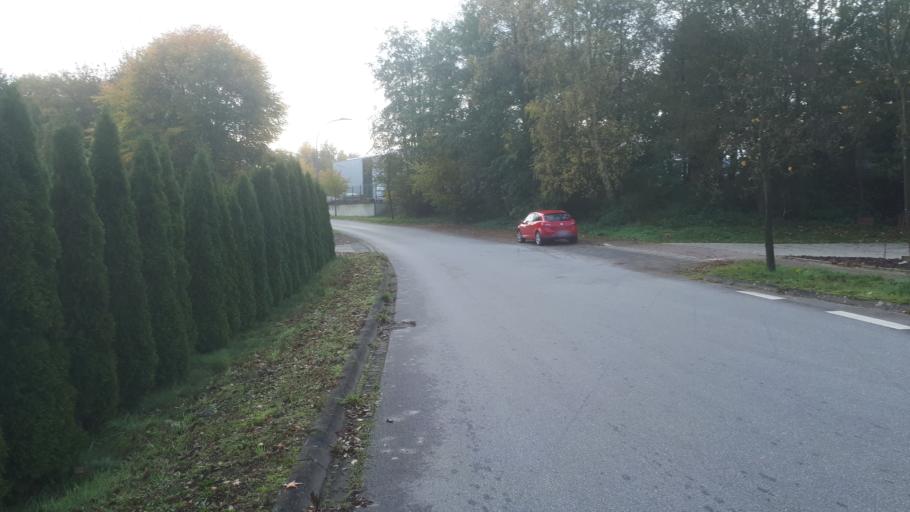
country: DE
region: North Rhine-Westphalia
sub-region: Regierungsbezirk Detmold
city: Huellhorst
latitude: 52.2676
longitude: 8.7078
